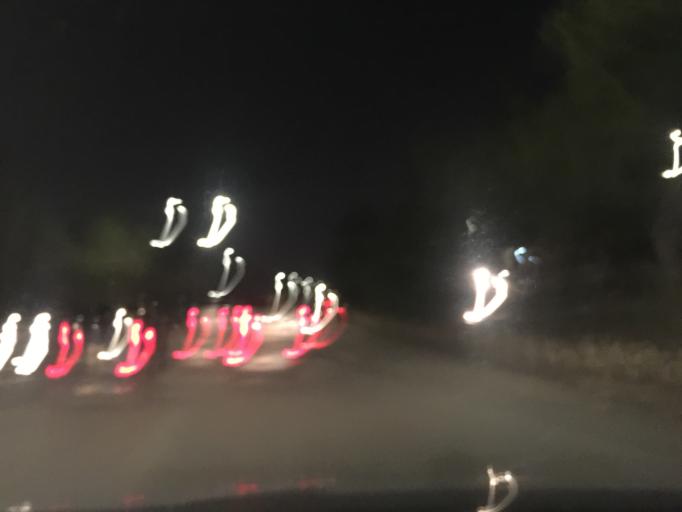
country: JO
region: Amman
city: Umm as Summaq
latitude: 31.9051
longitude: 35.8534
